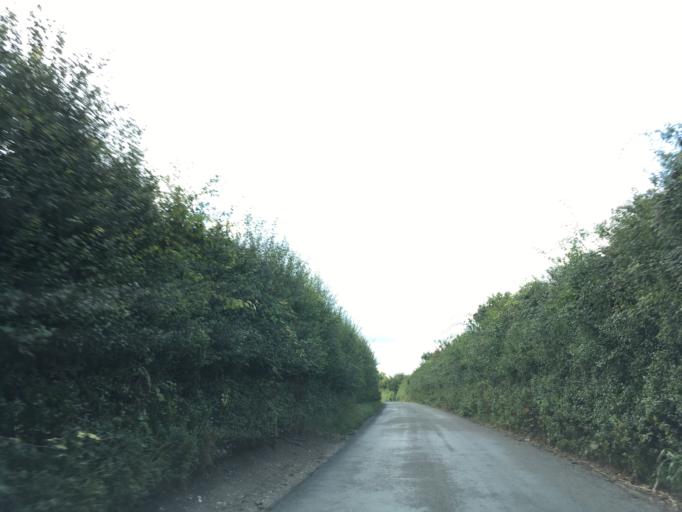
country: GB
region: England
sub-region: Hampshire
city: Andover
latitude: 51.1895
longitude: -1.3781
